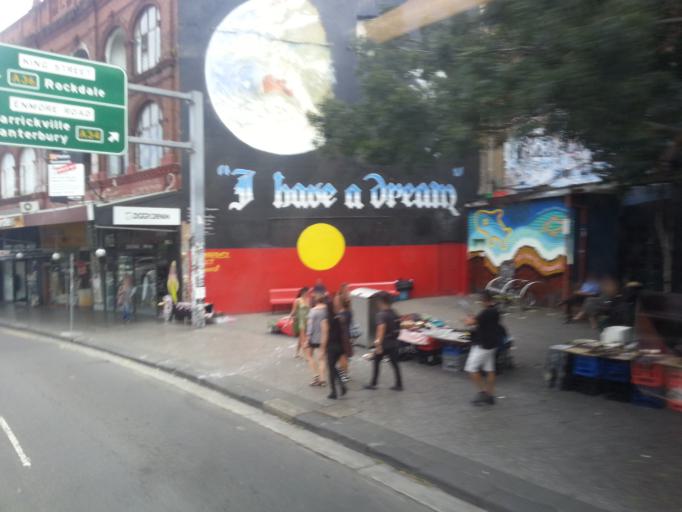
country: AU
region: New South Wales
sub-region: Marrickville
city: Newtown
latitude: -33.8967
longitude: 151.1796
